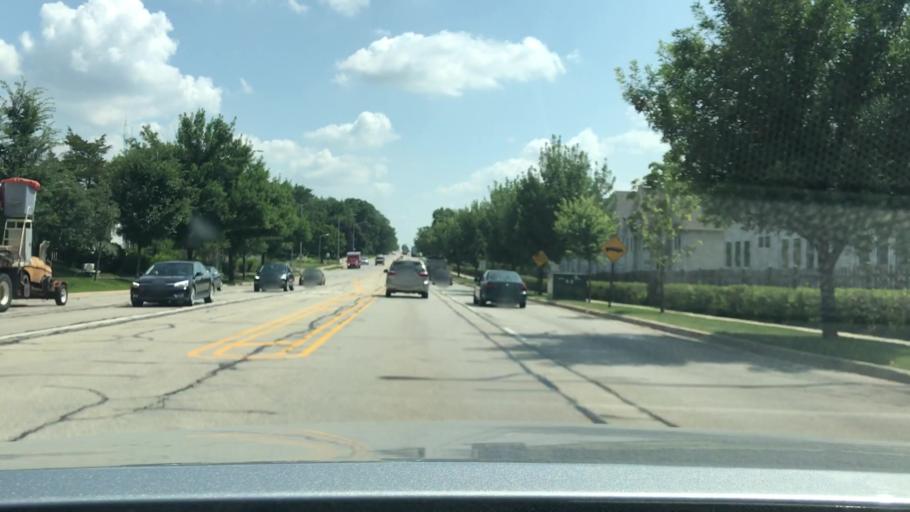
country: US
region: Illinois
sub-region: Will County
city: Bolingbrook
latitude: 41.7153
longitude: -88.0571
